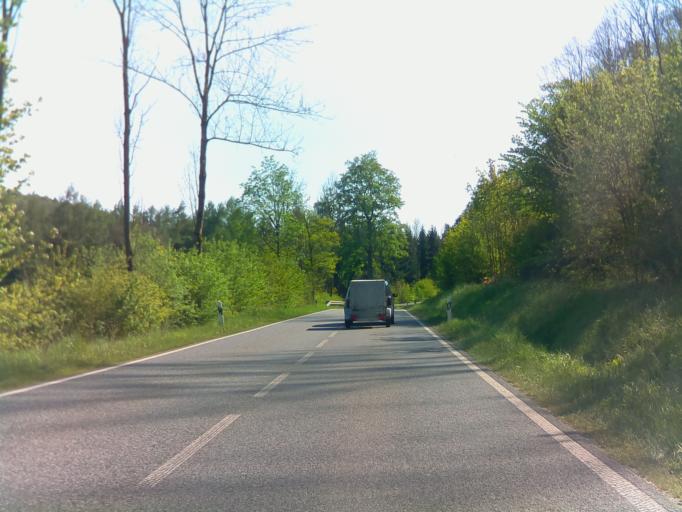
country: DE
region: Hesse
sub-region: Regierungsbezirk Darmstadt
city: Birstein
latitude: 50.3452
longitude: 9.3049
